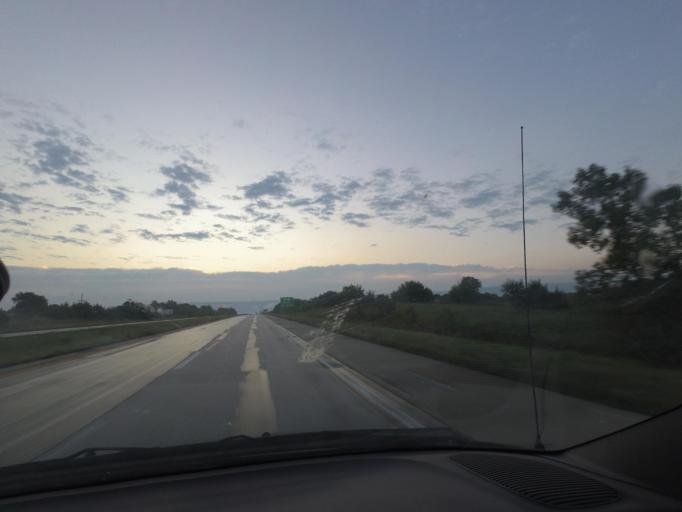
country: US
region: Missouri
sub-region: Macon County
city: Macon
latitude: 39.7606
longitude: -92.5775
